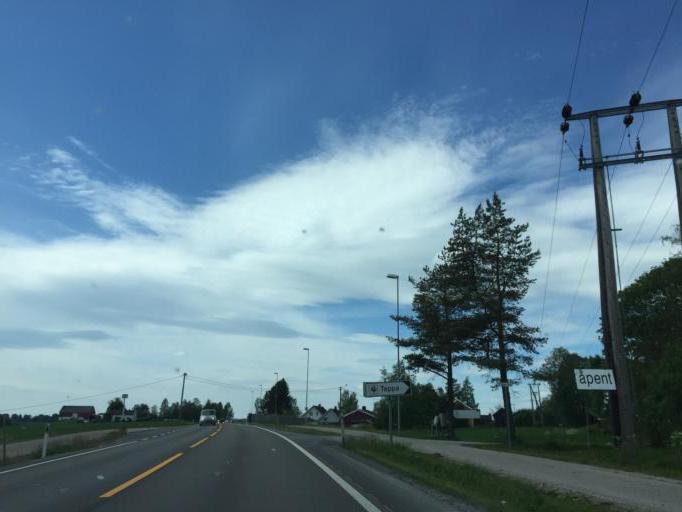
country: NO
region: Akershus
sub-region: Nes
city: Arnes
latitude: 60.1750
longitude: 11.4965
